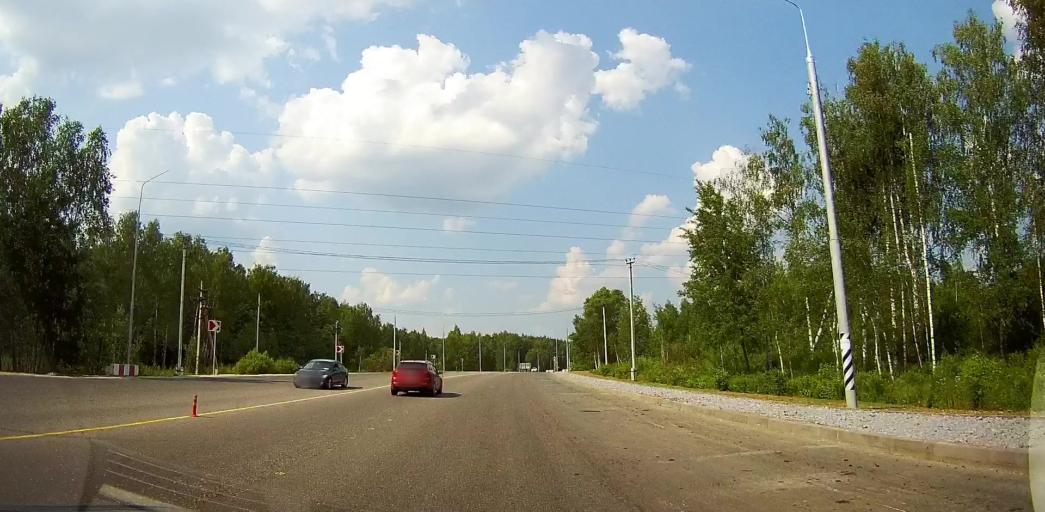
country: RU
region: Moskovskaya
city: Mikhnevo
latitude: 55.0737
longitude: 37.9516
